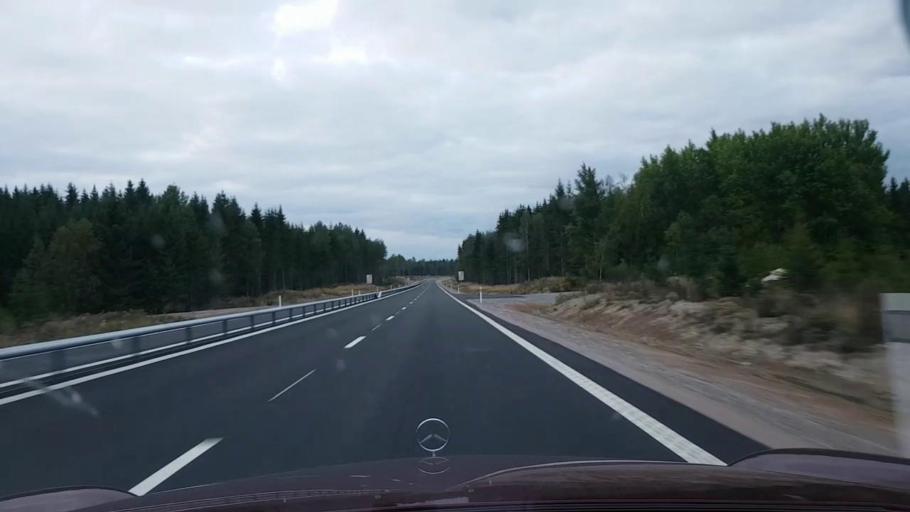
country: SE
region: Vaestmanland
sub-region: Hallstahammars Kommun
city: Hallstahammar
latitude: 59.6476
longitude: 16.2084
